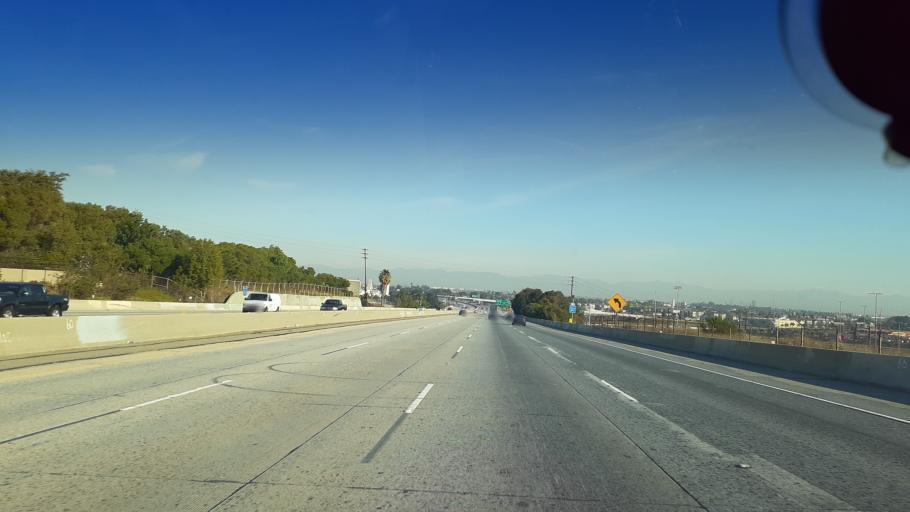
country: US
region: California
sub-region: Los Angeles County
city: San Pedro
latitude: 33.7644
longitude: -118.2829
